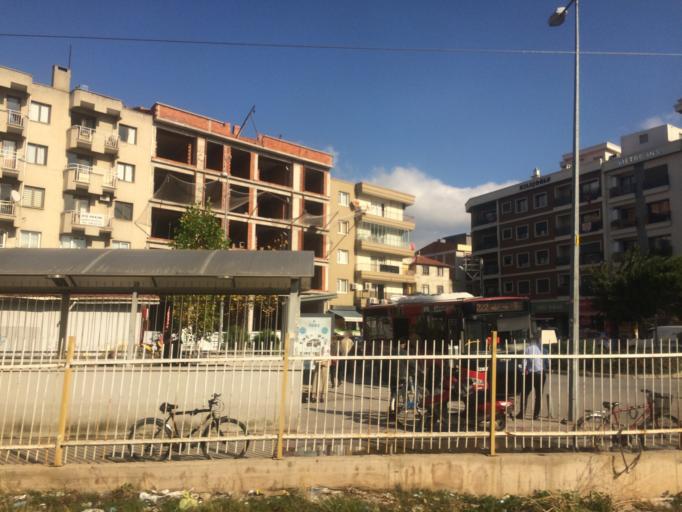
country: TR
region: Izmir
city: Karsiyaka
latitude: 38.4710
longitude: 27.0938
